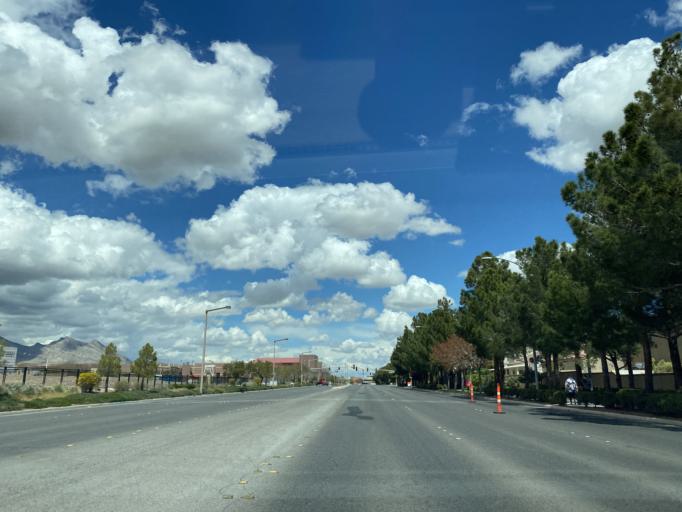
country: US
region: Nevada
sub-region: Clark County
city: Summerlin South
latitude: 36.1504
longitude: -115.3156
